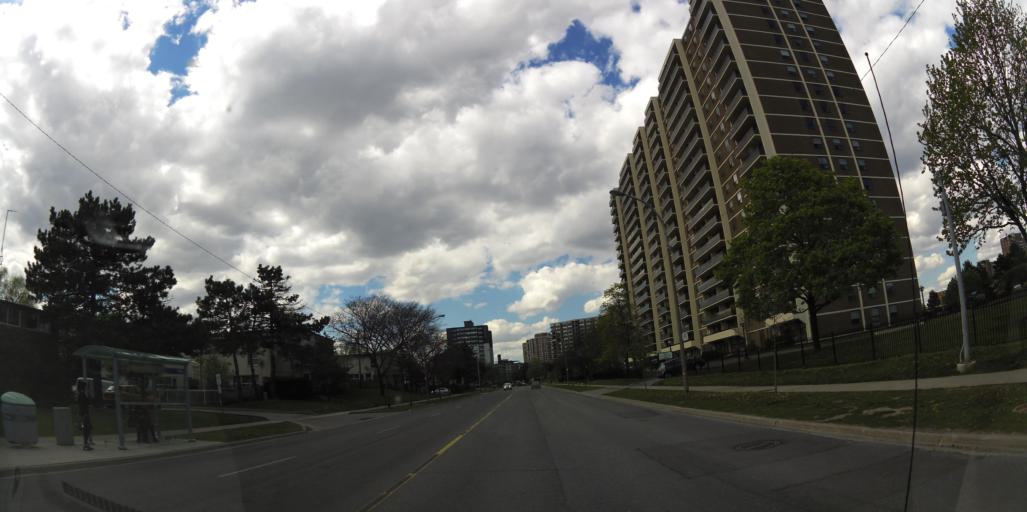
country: CA
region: Ontario
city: Etobicoke
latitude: 43.6497
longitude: -79.5687
